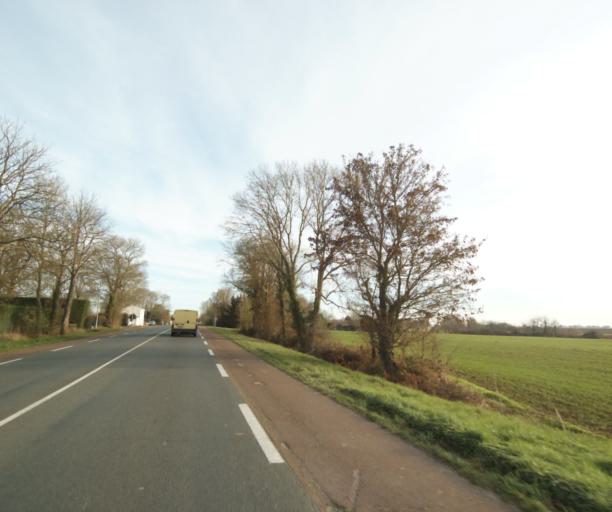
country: FR
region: Poitou-Charentes
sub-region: Departement de la Charente-Maritime
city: Saint-Georges-des-Coteaux
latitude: 45.7894
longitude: -0.7232
